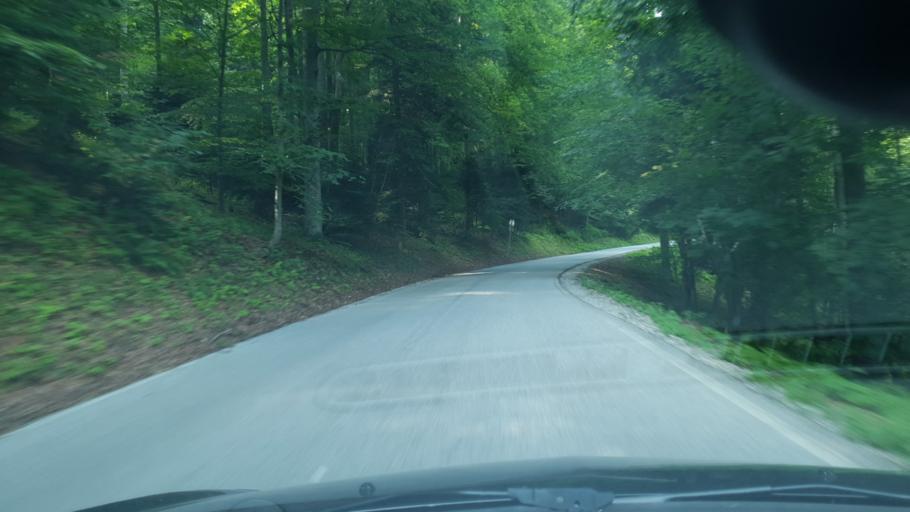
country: HR
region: Grad Zagreb
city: Kasina
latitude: 45.9012
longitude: 15.9606
